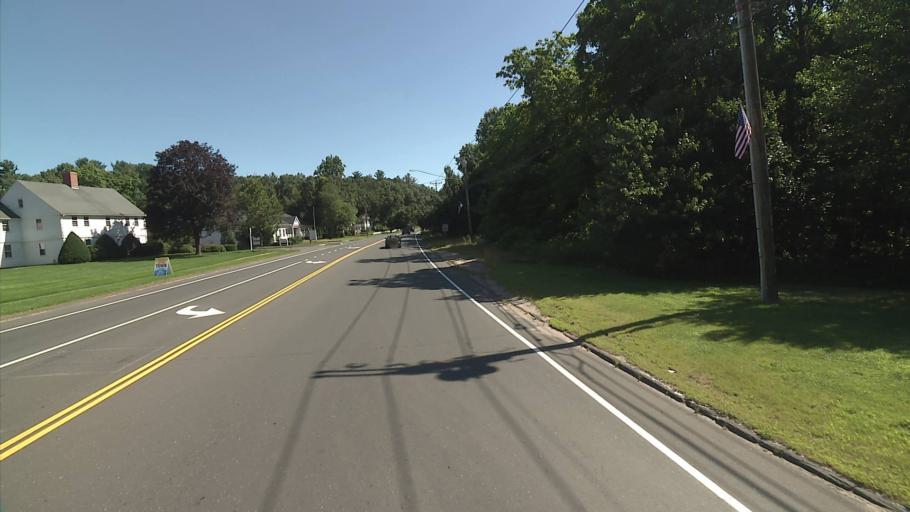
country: US
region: Connecticut
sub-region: Hartford County
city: Simsbury Center
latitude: 41.8852
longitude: -72.7986
